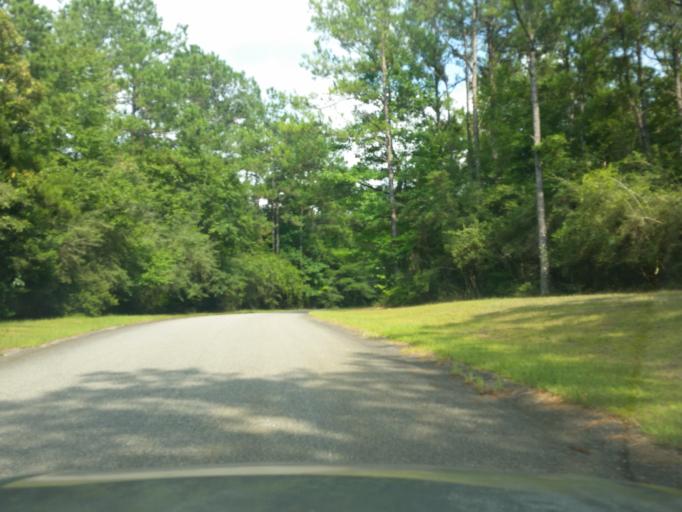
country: US
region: Alabama
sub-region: Baldwin County
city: Spanish Fort
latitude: 30.7350
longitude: -87.9055
